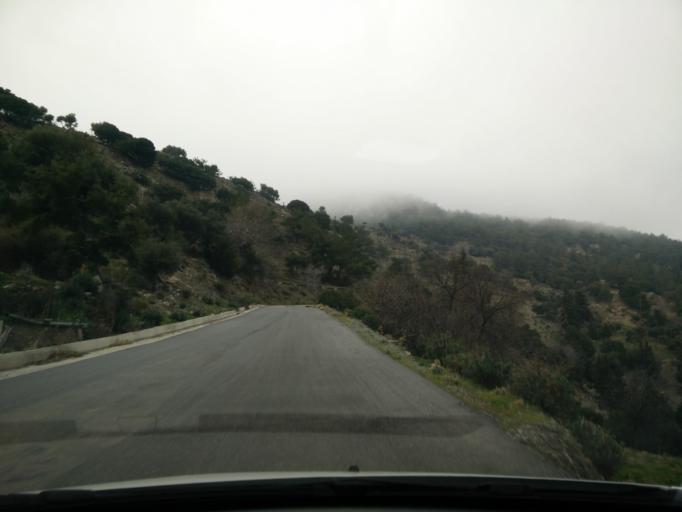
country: GR
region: Crete
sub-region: Nomos Lasithiou
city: Kritsa
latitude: 35.0410
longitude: 25.4853
